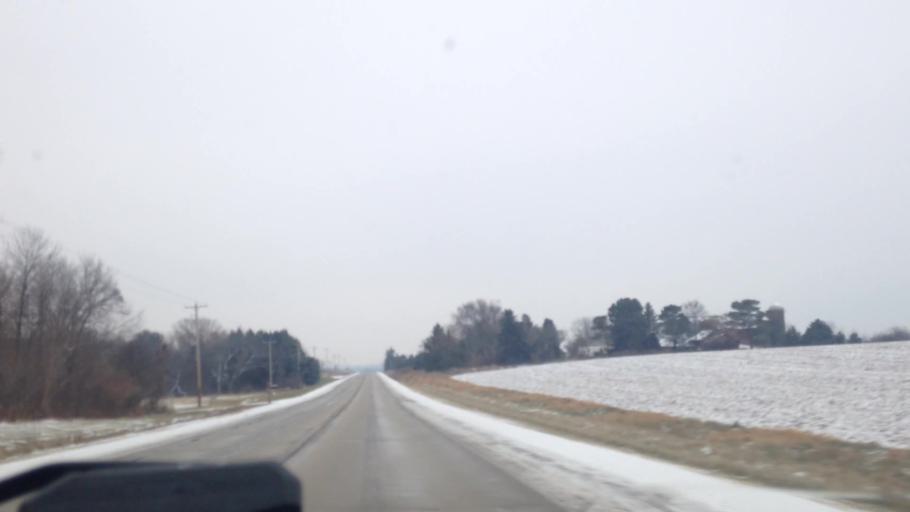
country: US
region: Wisconsin
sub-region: Dodge County
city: Hustisford
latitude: 43.2594
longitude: -88.5178
